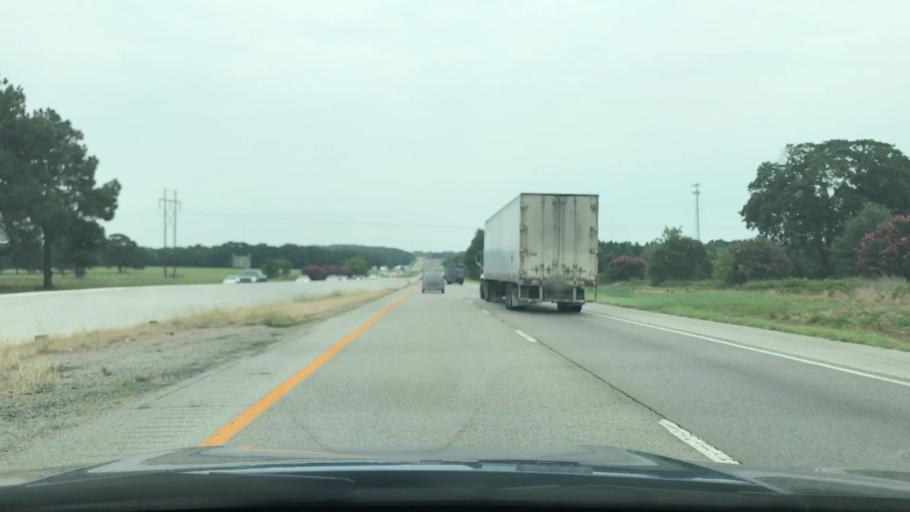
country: US
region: Texas
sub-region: Van Zandt County
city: Van
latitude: 32.4908
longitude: -95.5526
